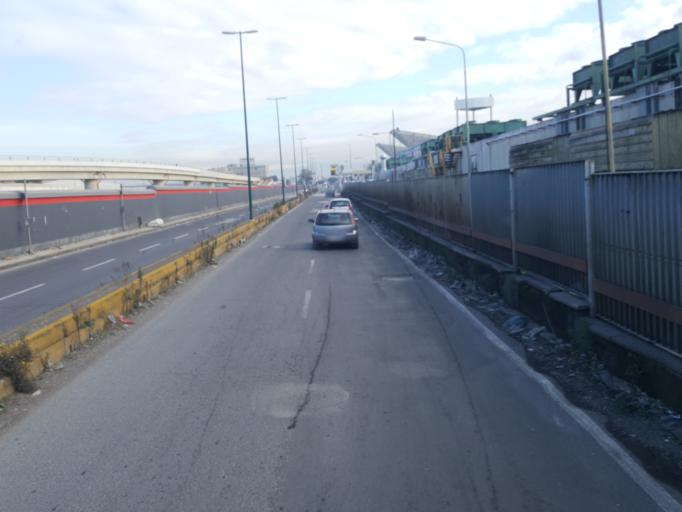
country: IT
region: Campania
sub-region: Provincia di Napoli
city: San Giorgio a Cremano
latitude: 40.8490
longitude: 14.3072
